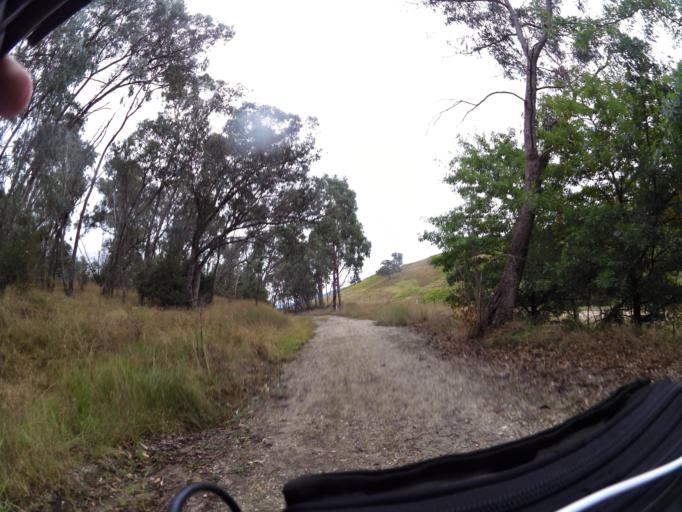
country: AU
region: New South Wales
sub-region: Greater Hume Shire
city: Holbrook
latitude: -36.1564
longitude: 147.4109
